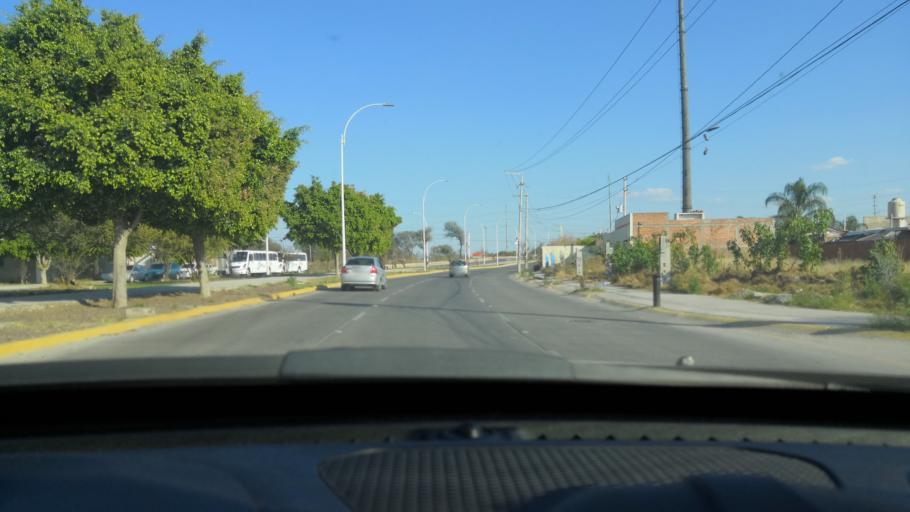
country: MX
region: Guanajuato
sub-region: Leon
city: Fraccionamiento Paraiso Real
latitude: 21.0599
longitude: -101.6114
